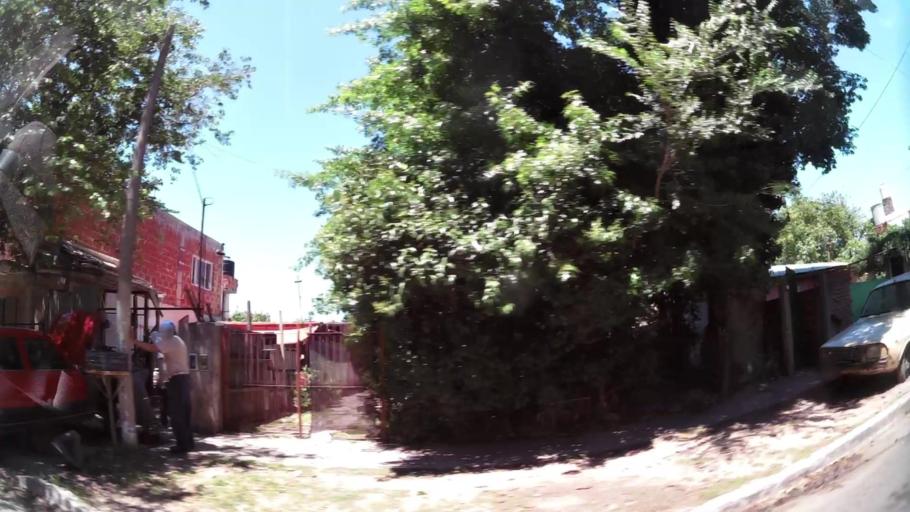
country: AR
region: Buenos Aires
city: Hurlingham
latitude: -34.5079
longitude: -58.7091
